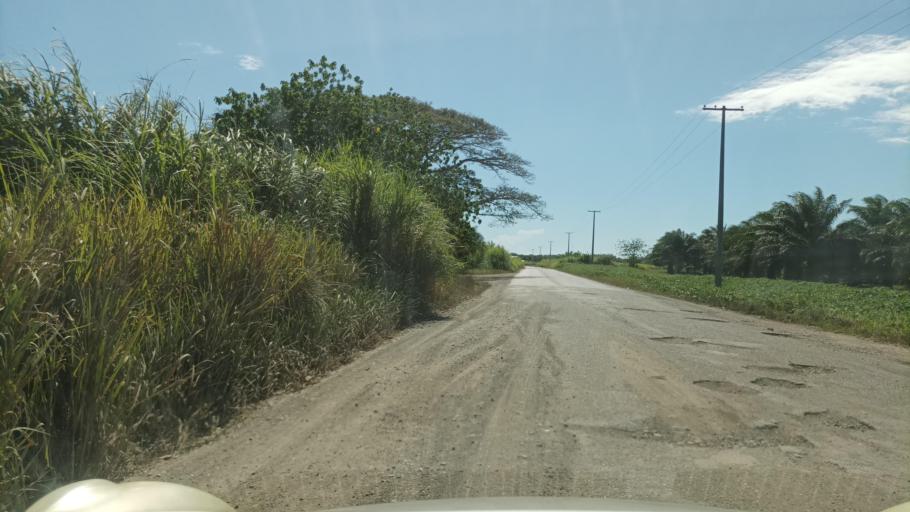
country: SB
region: Guadalcanal
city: Honiara
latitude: -9.4392
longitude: 160.1270
